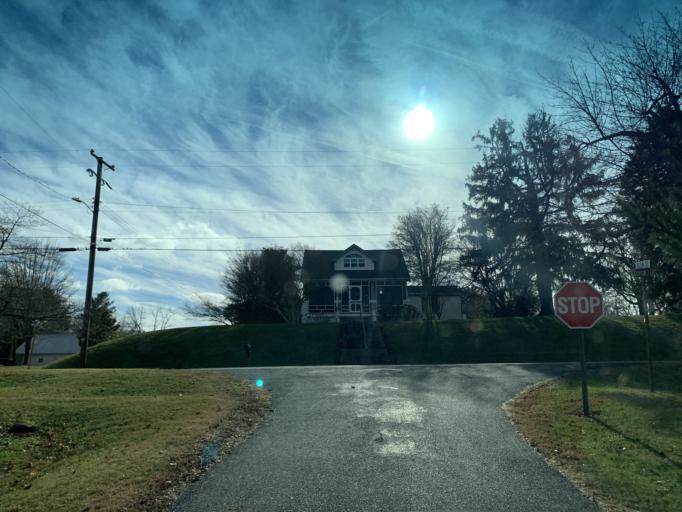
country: US
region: Maryland
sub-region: Harford County
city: Aberdeen Proving Ground
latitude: 39.3696
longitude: -76.0598
